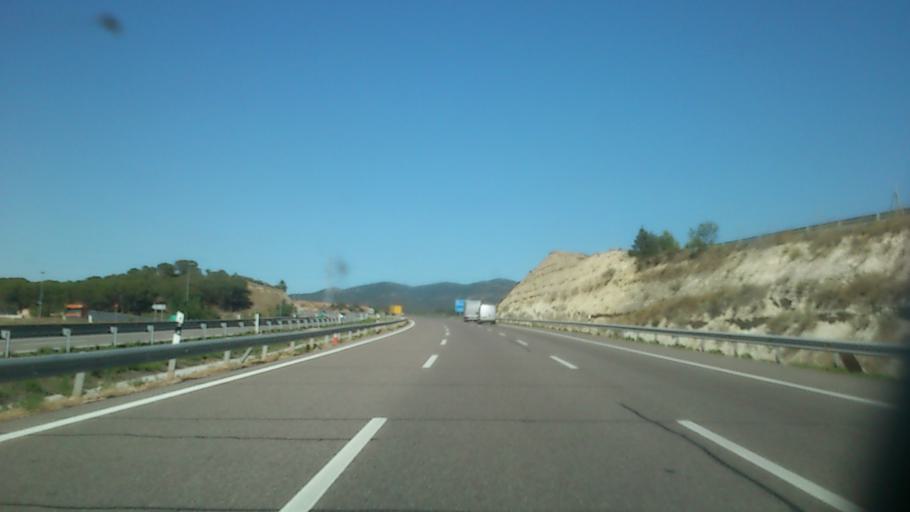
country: ES
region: Aragon
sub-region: Provincia de Zaragoza
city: Villalba de Perejil
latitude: 41.3638
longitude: -1.5876
